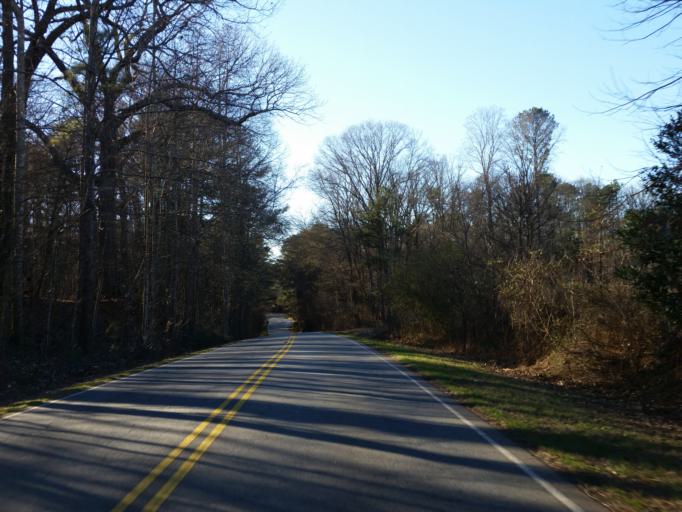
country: US
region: Georgia
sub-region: Cobb County
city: Marietta
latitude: 33.9642
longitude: -84.6017
